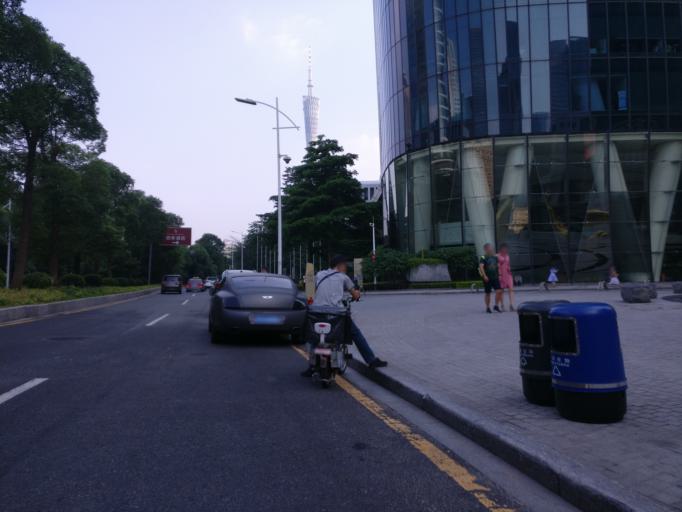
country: CN
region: Guangdong
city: Wushan
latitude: 23.1209
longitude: 113.3181
